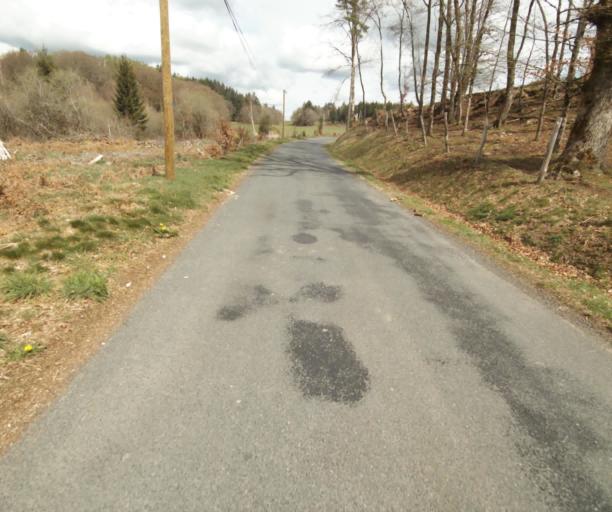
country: FR
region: Limousin
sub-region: Departement de la Correze
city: Correze
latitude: 45.3693
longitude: 1.9310
